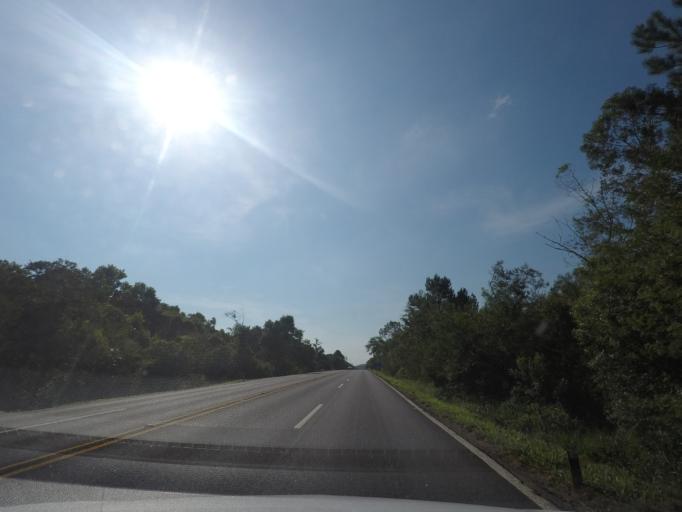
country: BR
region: Parana
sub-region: Paranagua
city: Paranagua
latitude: -25.5913
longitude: -48.6112
